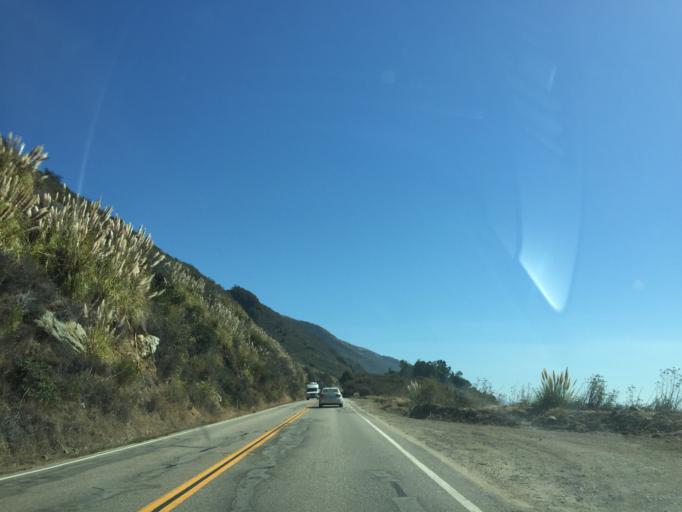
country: US
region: California
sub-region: Monterey County
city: Greenfield
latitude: 35.9989
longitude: -121.5003
